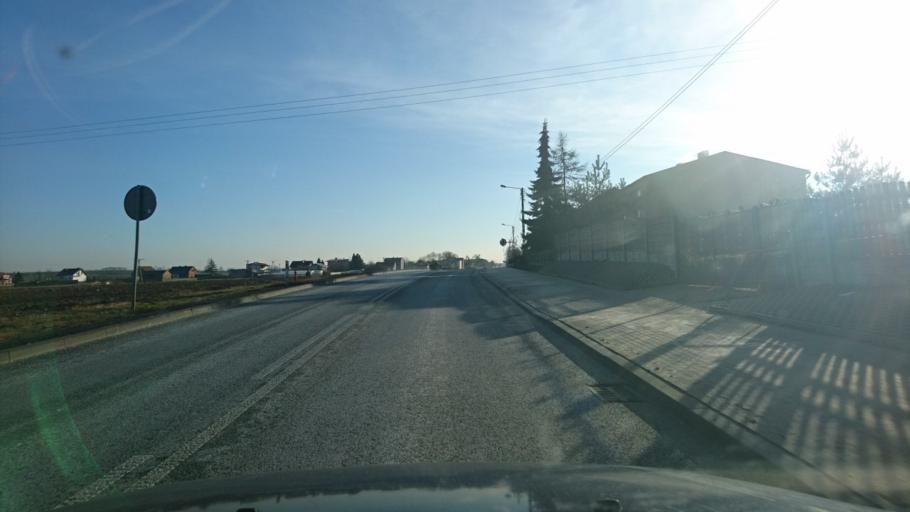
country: PL
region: Silesian Voivodeship
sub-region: Powiat klobucki
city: Starokrzepice
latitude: 51.0200
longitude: 18.6518
